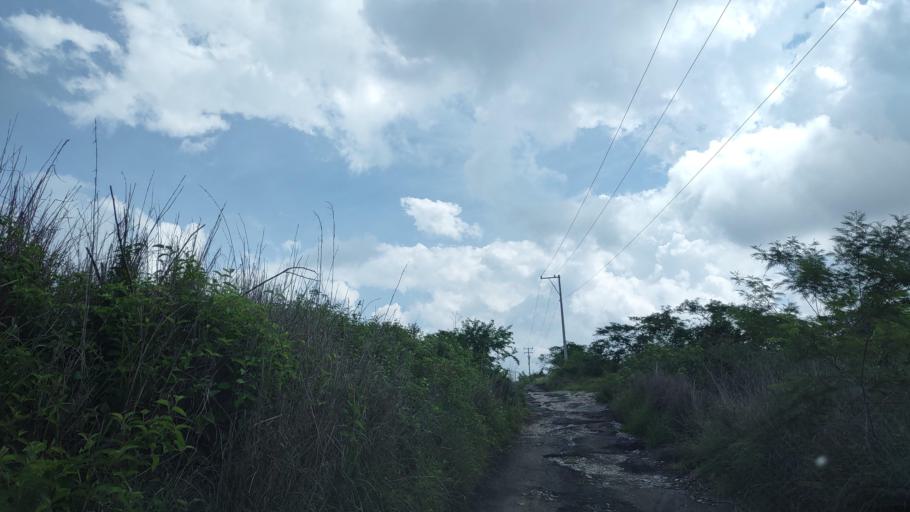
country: MX
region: Veracruz
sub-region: Emiliano Zapata
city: Dos Rios
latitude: 19.4532
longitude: -96.8089
